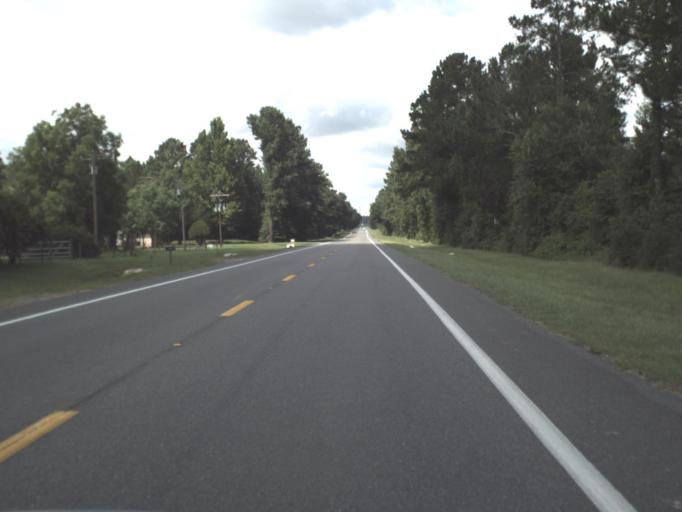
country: US
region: Florida
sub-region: Union County
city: Lake Butler
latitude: 29.9947
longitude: -82.3785
